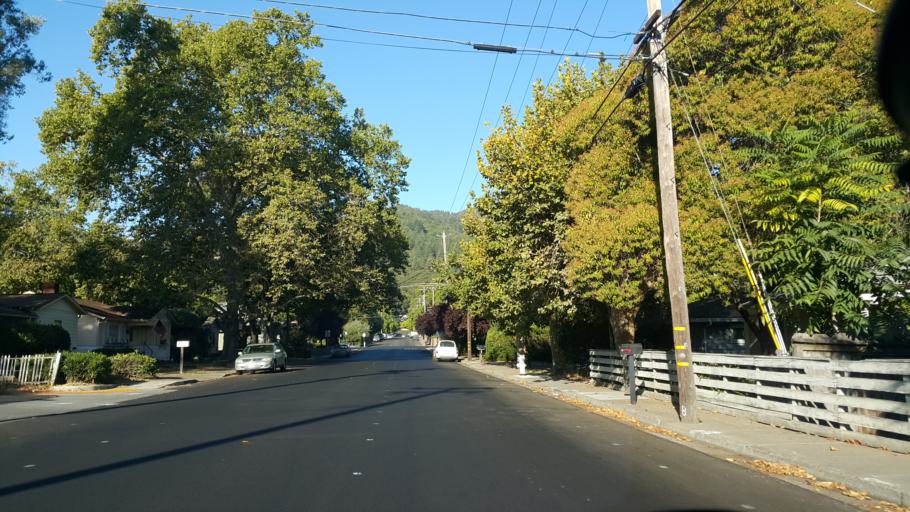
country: US
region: California
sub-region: Mendocino County
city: Ukiah
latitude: 39.1342
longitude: -123.2076
